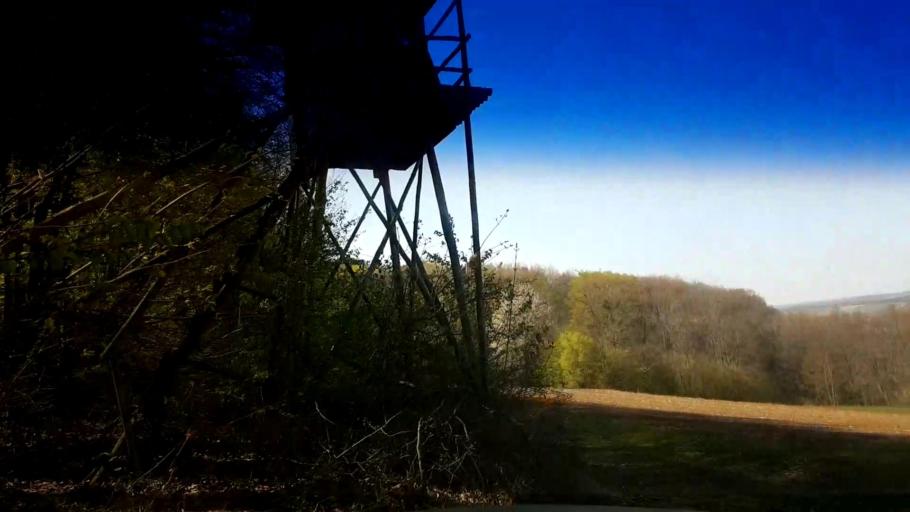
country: DE
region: Bavaria
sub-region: Upper Franconia
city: Schesslitz
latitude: 49.9418
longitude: 11.0463
